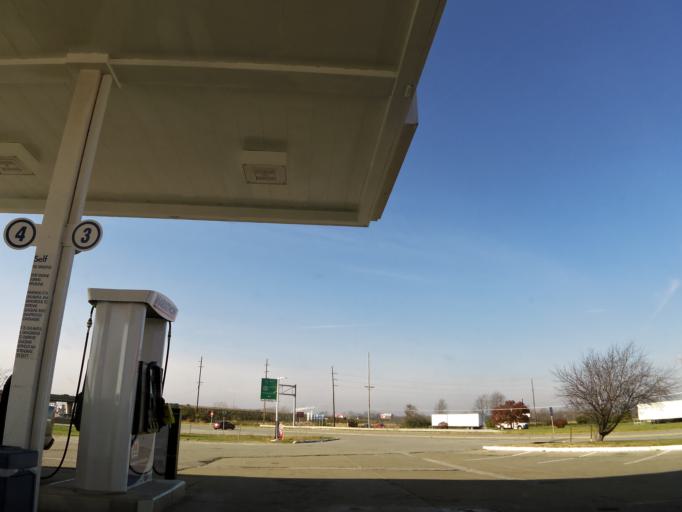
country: US
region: Indiana
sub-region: Shelby County
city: Shelbyville
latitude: 39.5270
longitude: -85.7333
